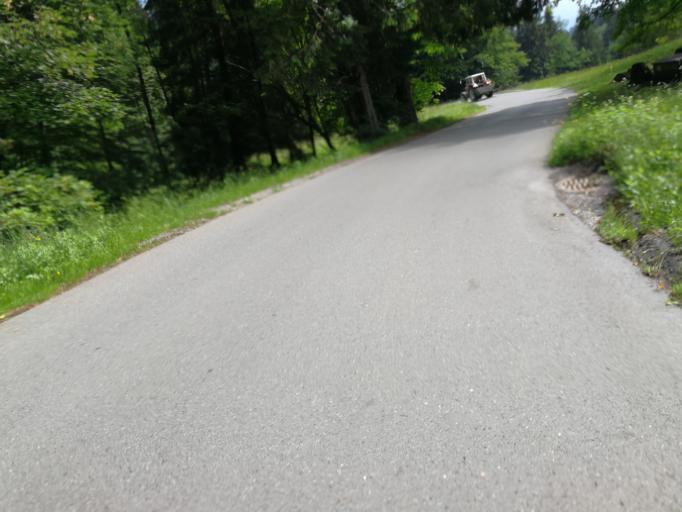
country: CH
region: Schwyz
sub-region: Bezirk Hoefe
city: Feusisberg
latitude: 47.1746
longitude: 8.7725
